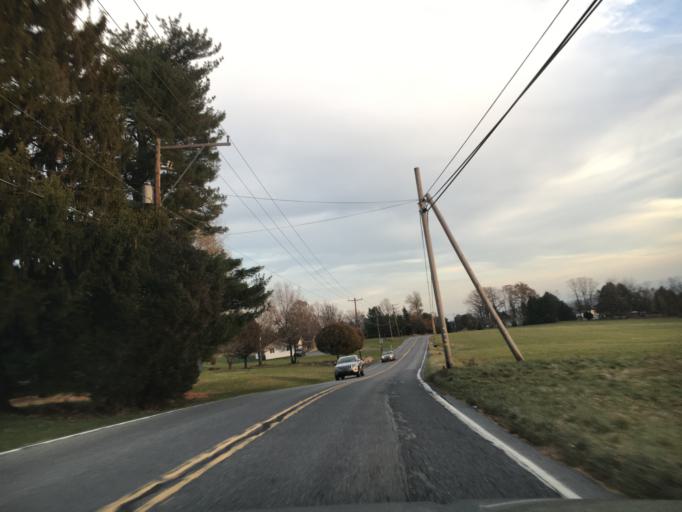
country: US
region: Pennsylvania
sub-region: Lehigh County
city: Slatington
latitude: 40.7173
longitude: -75.5996
